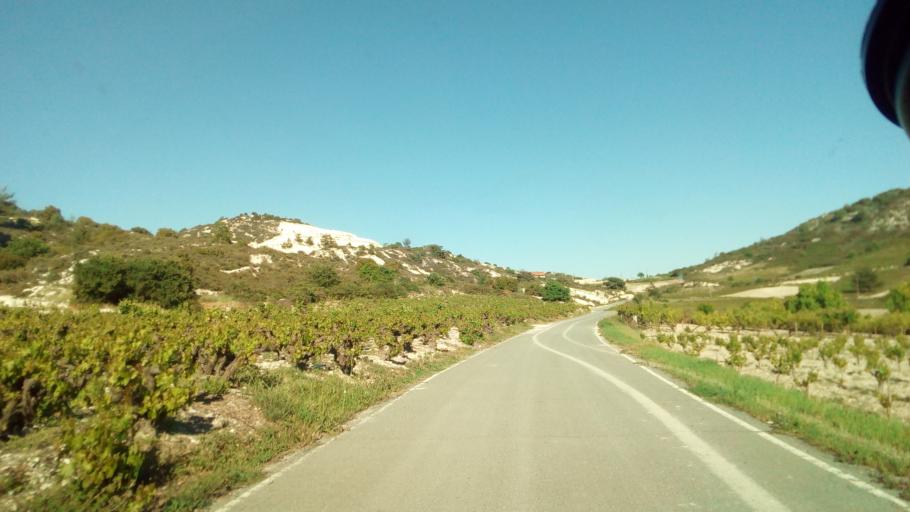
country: CY
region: Limassol
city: Pachna
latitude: 34.8647
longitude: 32.7932
